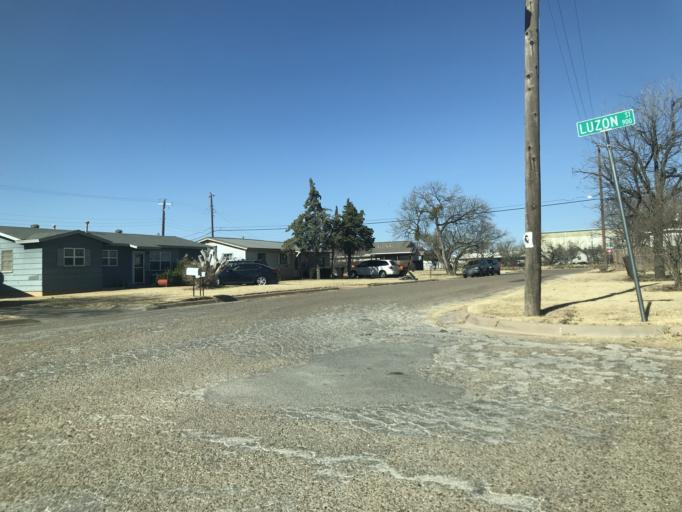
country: US
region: Texas
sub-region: Taylor County
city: Abilene
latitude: 32.4429
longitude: -99.7102
